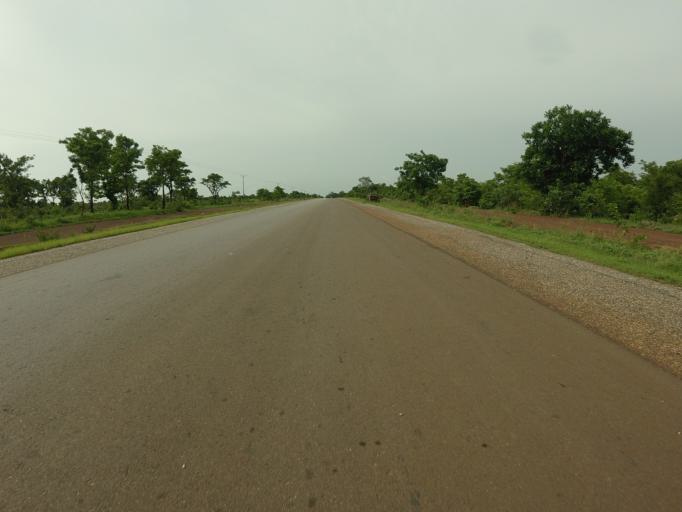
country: GH
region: Northern
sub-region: Yendi
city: Yendi
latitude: 9.6467
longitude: -0.0684
